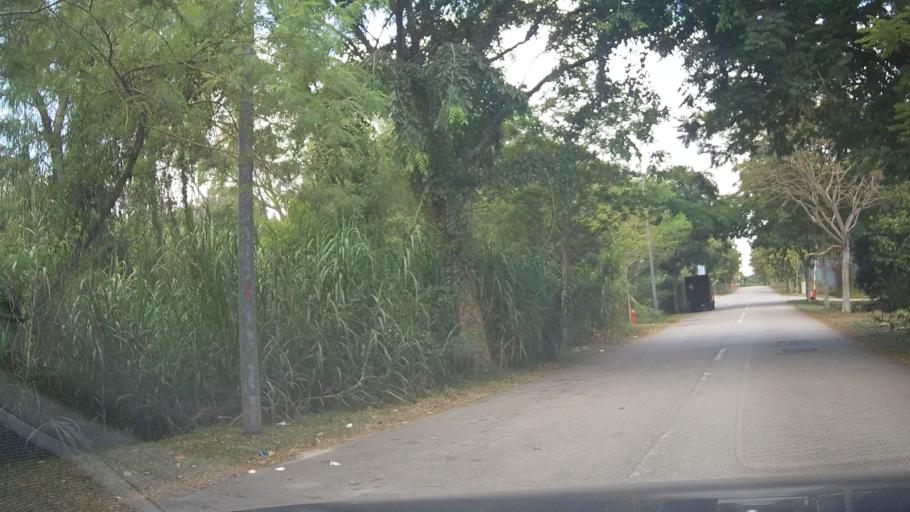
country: SG
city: Singapore
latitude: 1.3593
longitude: 103.9784
